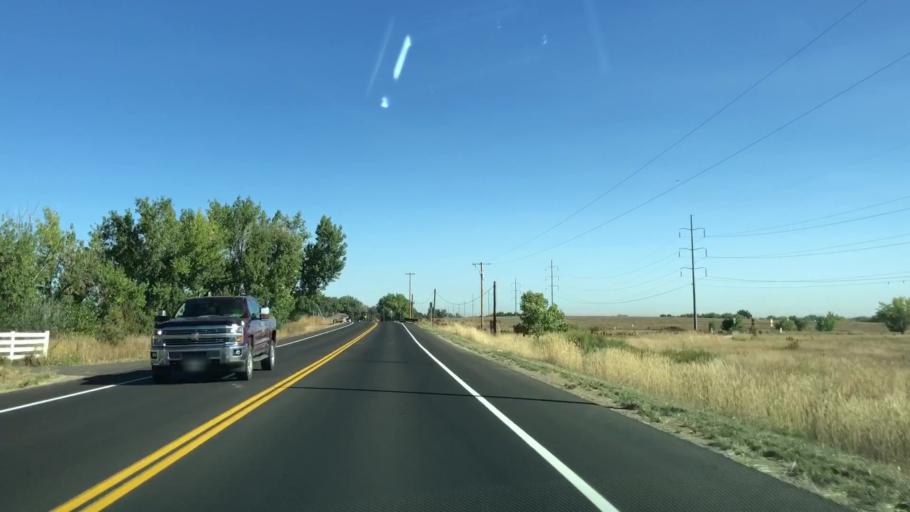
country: US
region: Colorado
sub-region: Larimer County
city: Loveland
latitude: 40.4375
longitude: -105.0454
